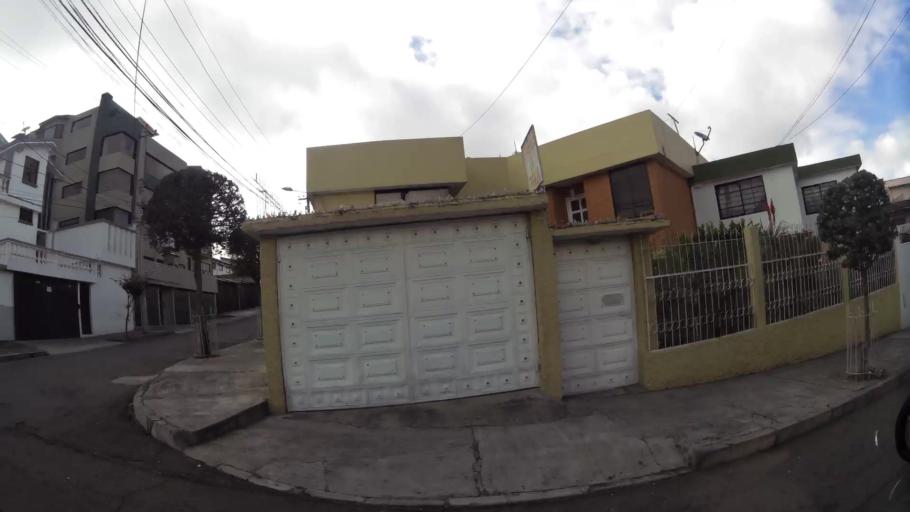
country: EC
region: Pichincha
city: Quito
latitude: -0.1597
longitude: -78.4707
